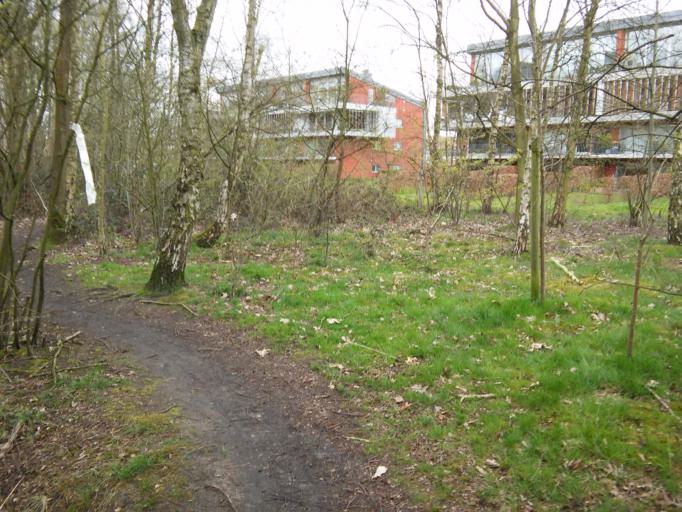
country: BE
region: Flanders
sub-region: Provincie Antwerpen
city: Boom
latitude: 51.0988
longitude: 4.3811
